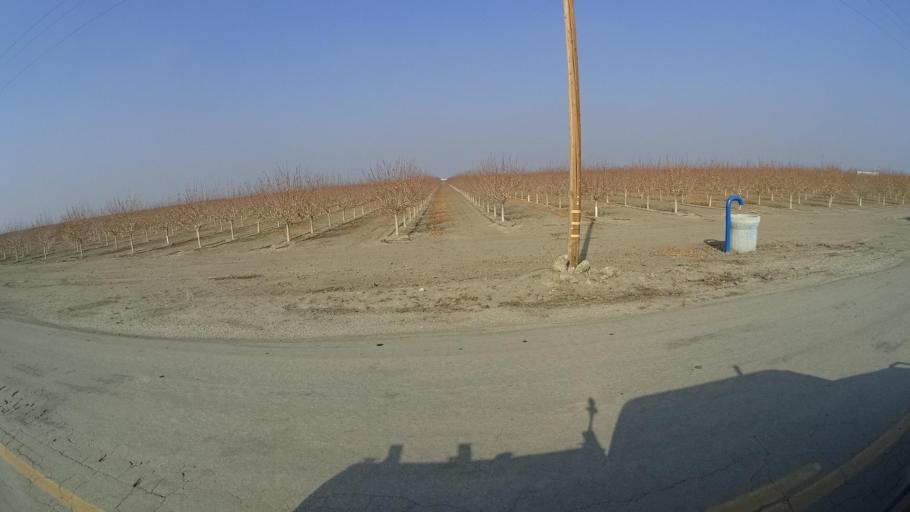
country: US
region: California
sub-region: Kern County
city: Greenfield
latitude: 35.1519
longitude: -119.1037
